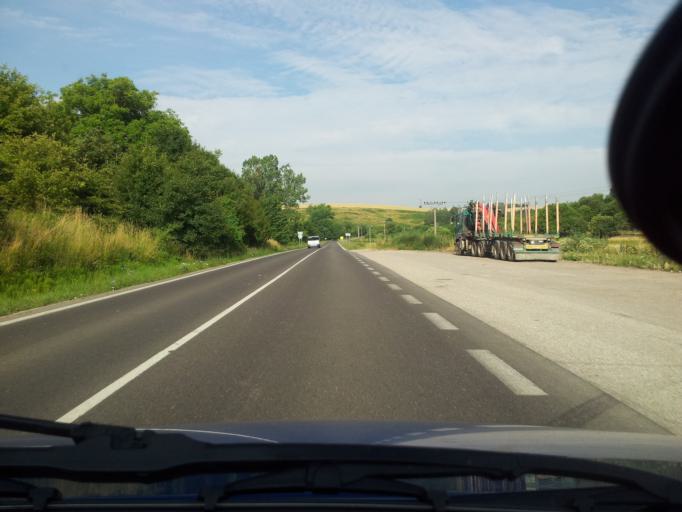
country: SK
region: Nitriansky
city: Banovce nad Bebravou
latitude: 48.6929
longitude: 18.3154
